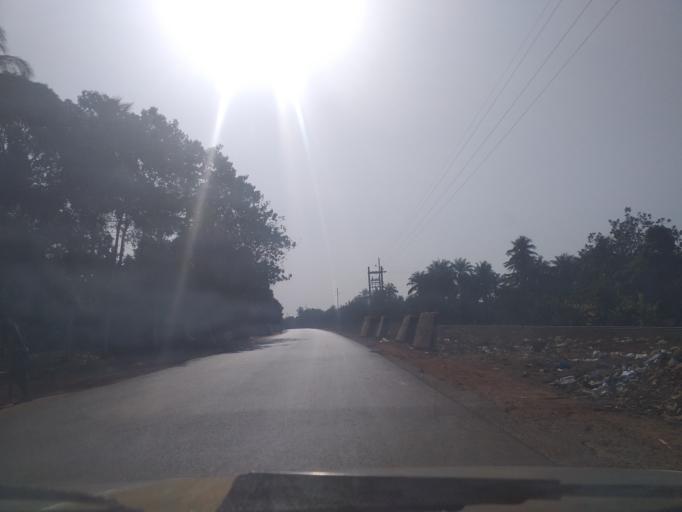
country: GN
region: Boke
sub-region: Boke Prefecture
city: Sangueya
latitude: 10.7776
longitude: -14.4395
